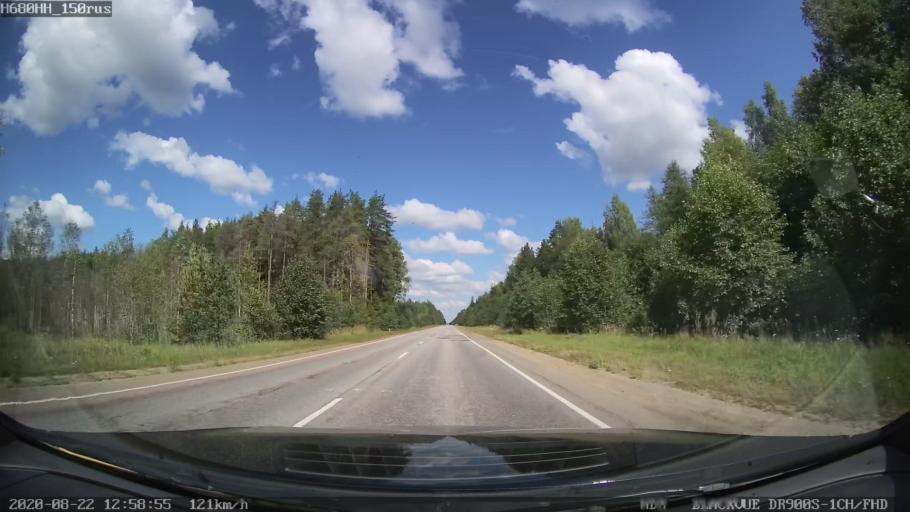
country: RU
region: Tverskaya
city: Bezhetsk
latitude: 57.5976
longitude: 36.3523
